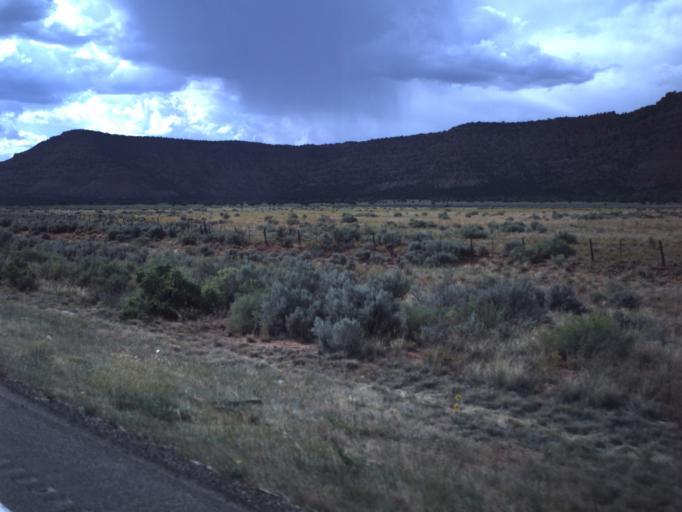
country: US
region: Utah
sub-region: Kane County
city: Kanab
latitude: 37.0359
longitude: -112.3777
